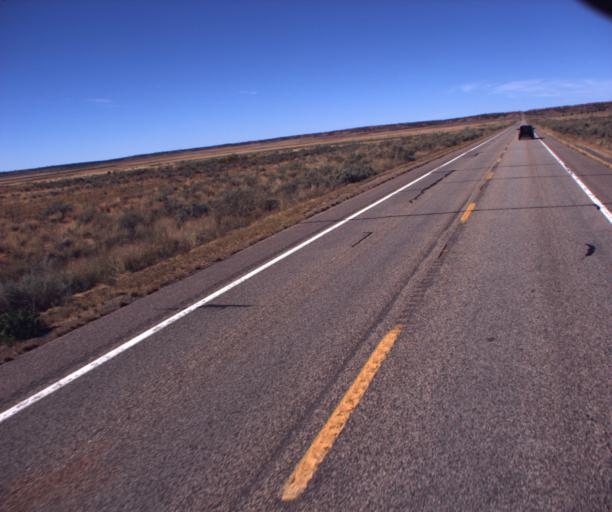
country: US
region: Arizona
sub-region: Mohave County
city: Colorado City
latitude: 36.8676
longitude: -112.8439
